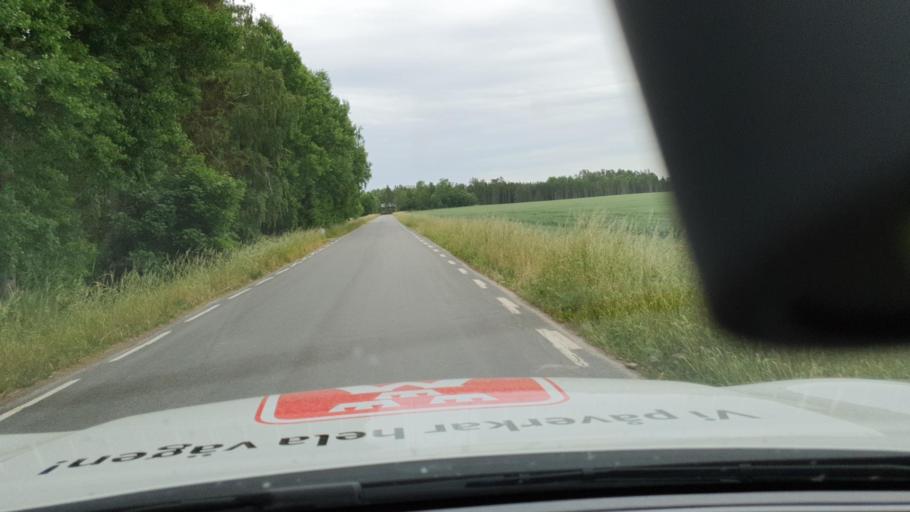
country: SE
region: Vaestra Goetaland
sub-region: Tibro Kommun
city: Tibro
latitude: 58.3432
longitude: 14.1082
